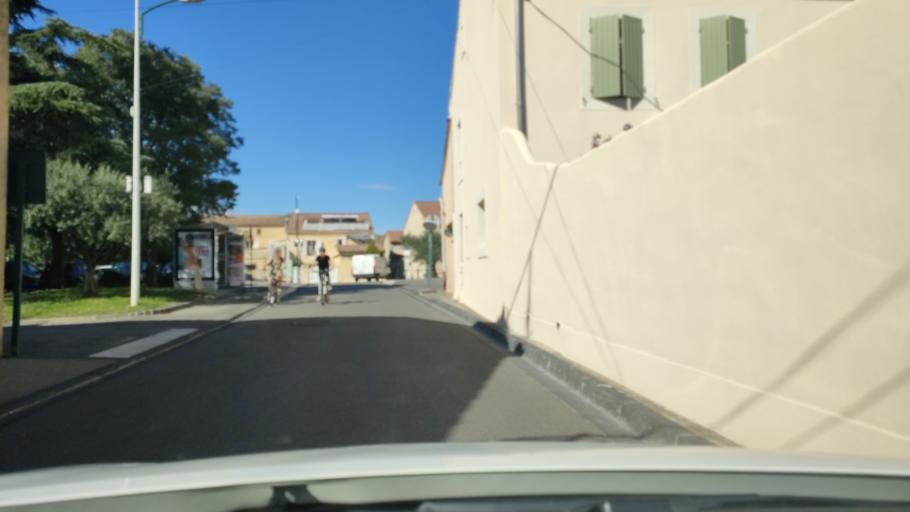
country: FR
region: Provence-Alpes-Cote d'Azur
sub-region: Departement du Vaucluse
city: Morieres-les-Avignon
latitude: 43.9407
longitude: 4.9036
